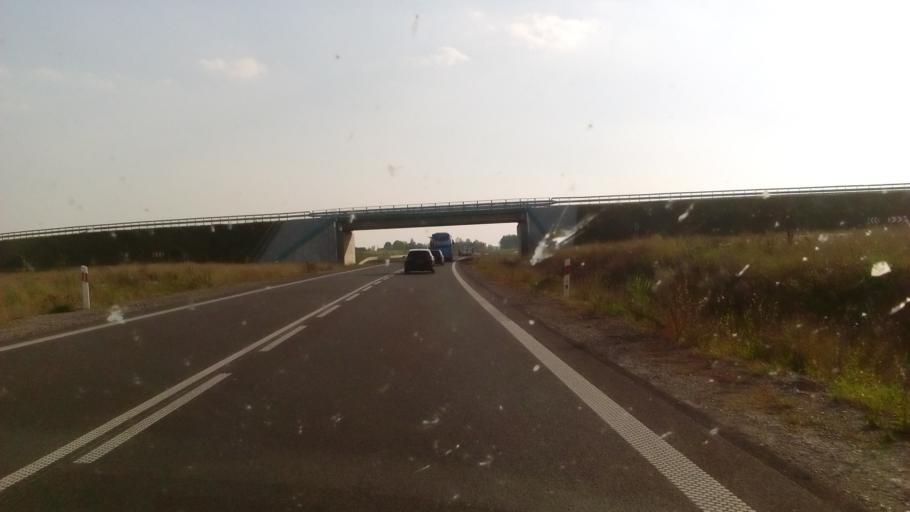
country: PL
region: Podlasie
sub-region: Powiat grajewski
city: Rajgrod
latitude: 53.7661
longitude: 22.8310
